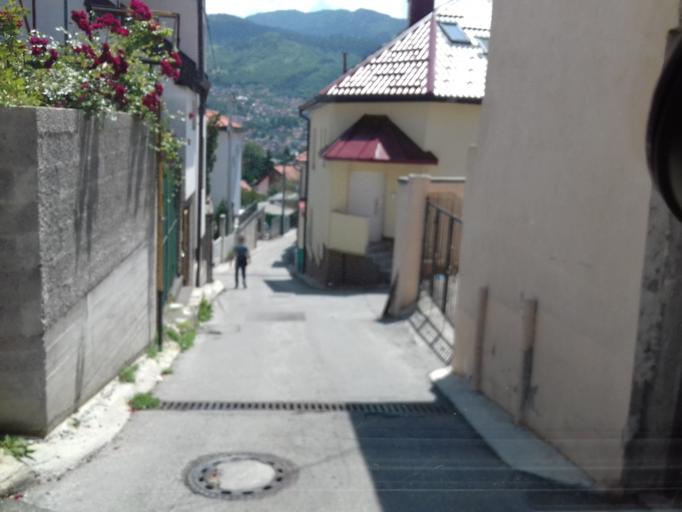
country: BA
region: Federation of Bosnia and Herzegovina
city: Kobilja Glava
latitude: 43.8662
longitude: 18.4235
